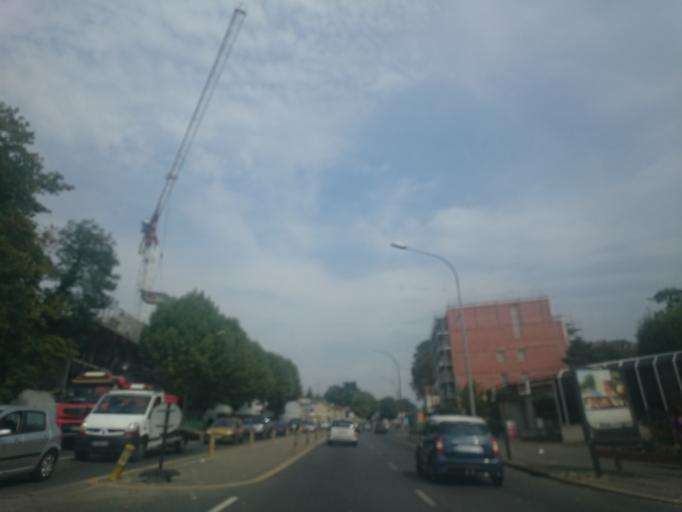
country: FR
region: Ile-de-France
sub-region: Departement de l'Essonne
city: Juvisy-sur-Orge
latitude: 48.6886
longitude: 2.3714
